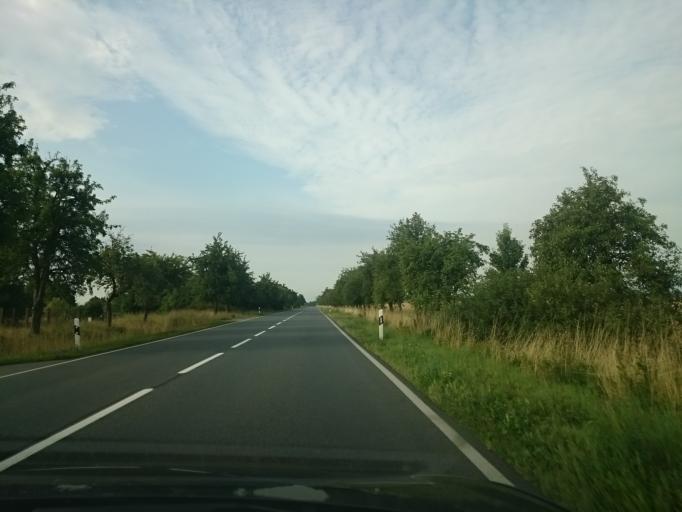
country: DE
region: Mecklenburg-Vorpommern
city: Wackerow
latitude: 53.7344
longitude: 12.9242
